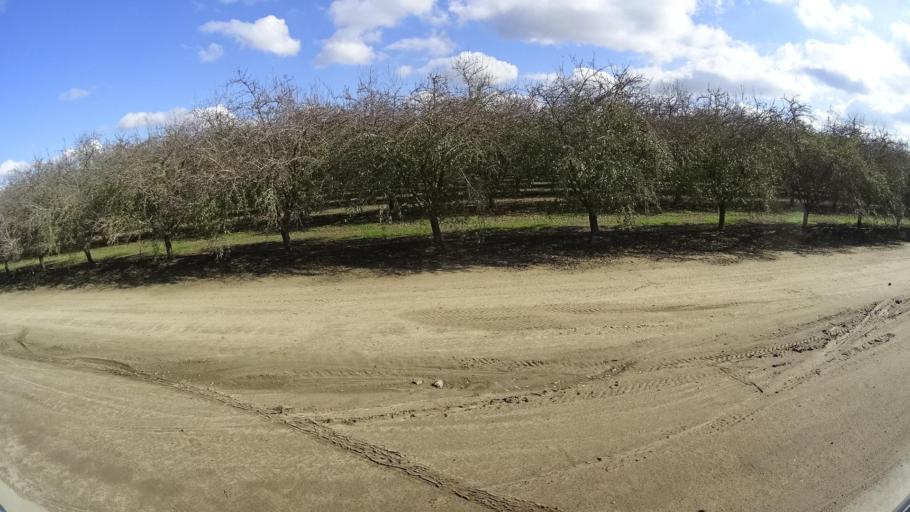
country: US
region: California
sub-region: Kern County
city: McFarland
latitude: 35.7130
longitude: -119.2408
